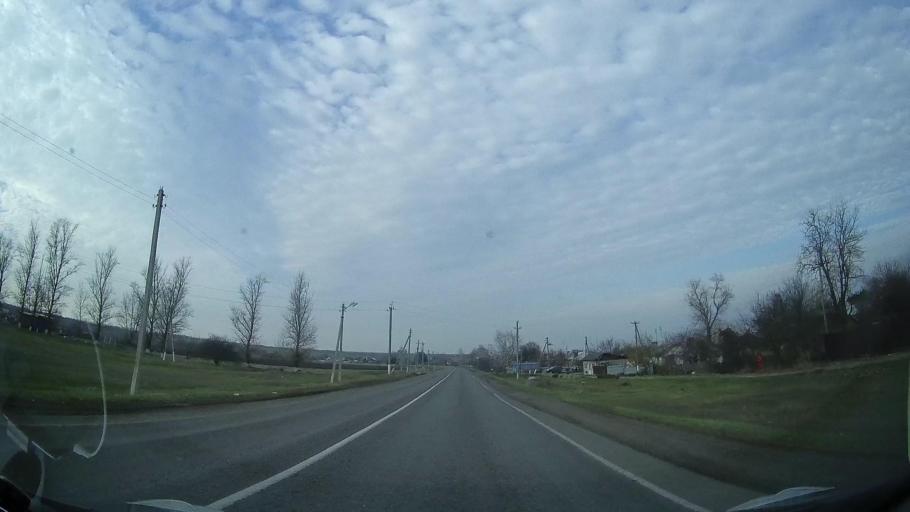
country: RU
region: Rostov
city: Bagayevskaya
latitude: 47.0933
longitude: 40.3154
